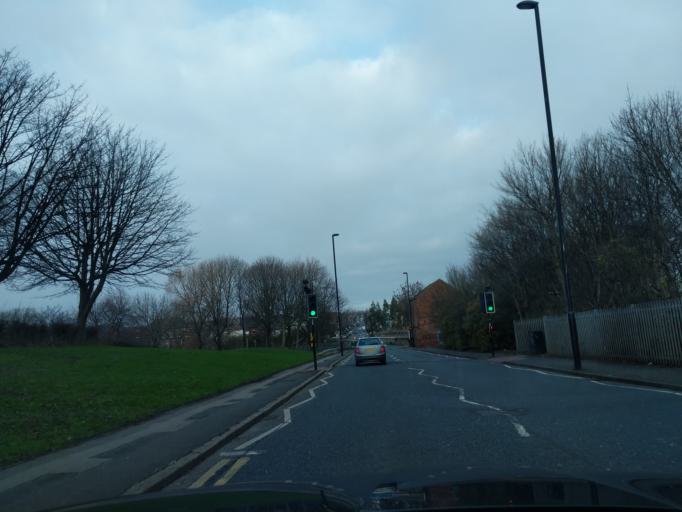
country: GB
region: England
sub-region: Gateshead
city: Felling
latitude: 54.9809
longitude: -1.5747
